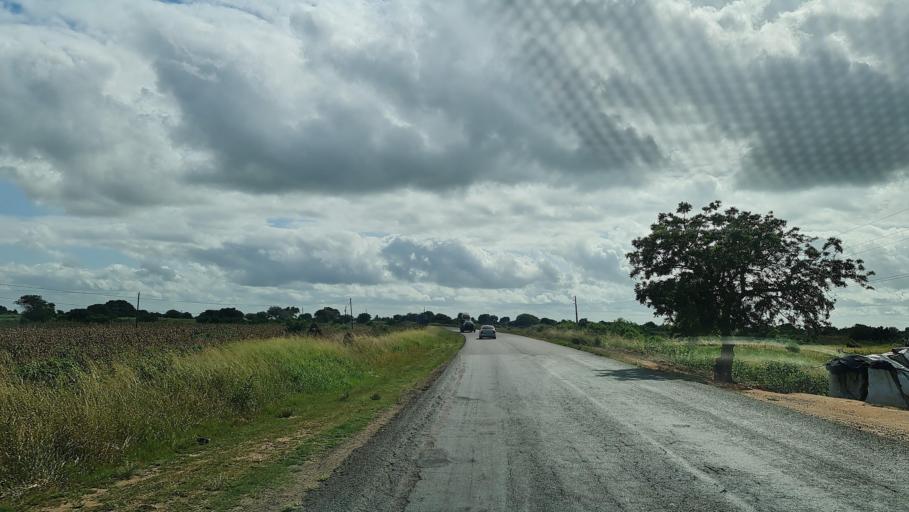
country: MZ
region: Gaza
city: Macia
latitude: -25.0897
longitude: 32.8412
